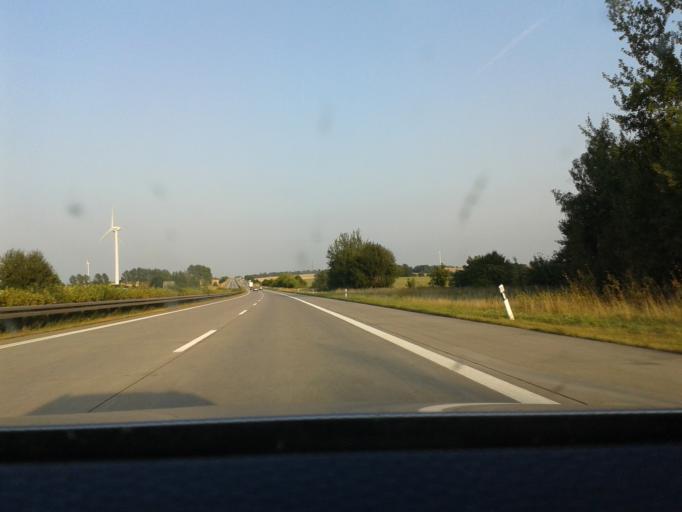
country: DE
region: Saxony
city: Bockelwitz
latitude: 51.1954
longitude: 12.9793
